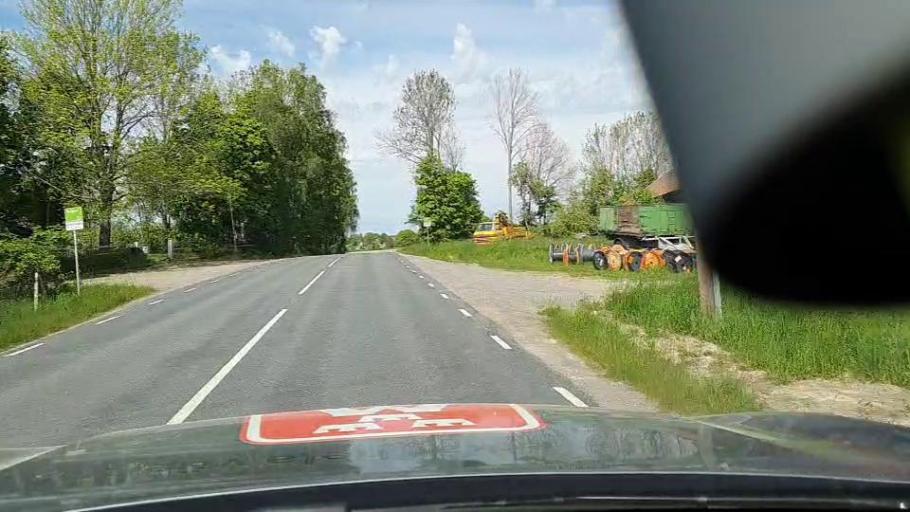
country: SE
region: Soedermanland
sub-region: Eskilstuna Kommun
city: Skogstorp
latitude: 59.3079
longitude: 16.4630
